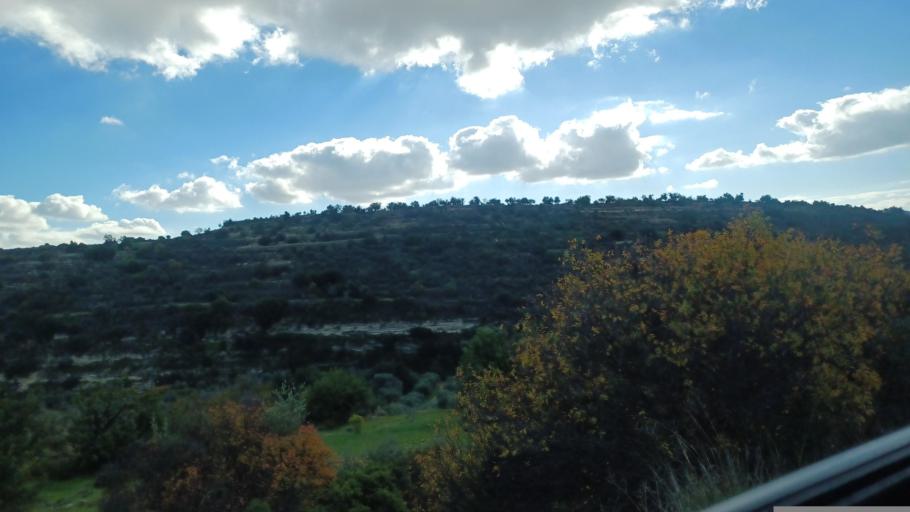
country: CY
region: Limassol
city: Pano Polemidia
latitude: 34.7649
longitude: 32.9793
